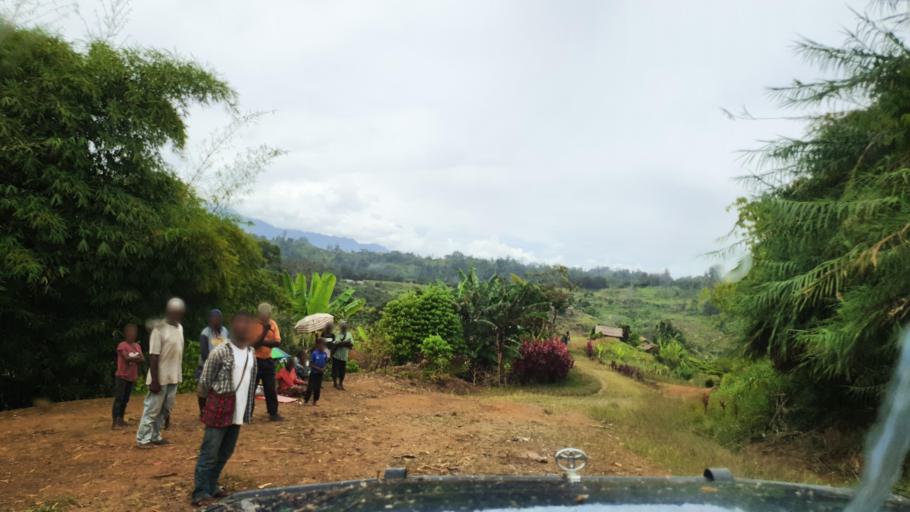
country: PG
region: Jiwaka
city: Minj
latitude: -5.9501
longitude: 144.7717
